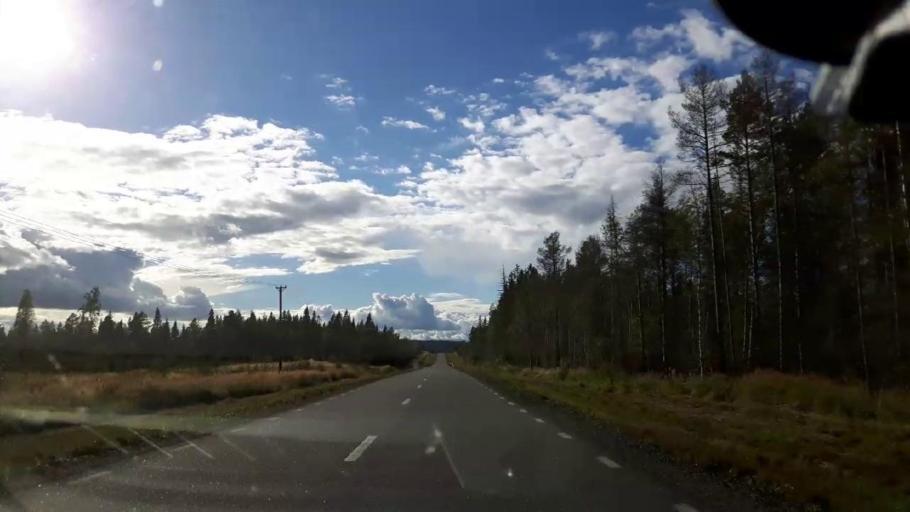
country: SE
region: Jaemtland
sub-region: Stroemsunds Kommun
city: Stroemsund
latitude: 63.5526
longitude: 15.8553
